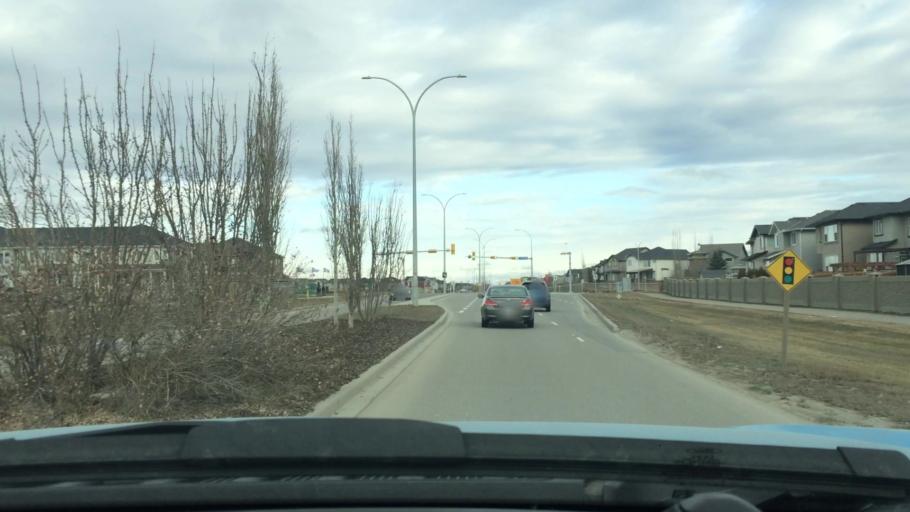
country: CA
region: Alberta
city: Airdrie
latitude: 51.2518
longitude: -114.0251
